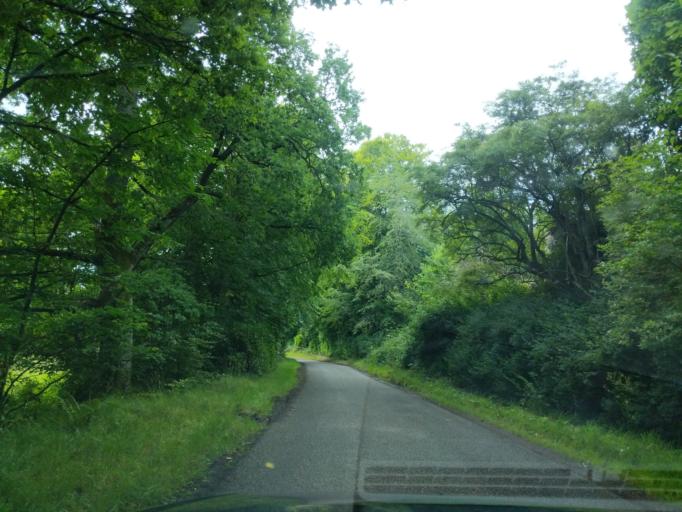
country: GB
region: Scotland
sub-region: Aberdeenshire
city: Aboyne
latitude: 57.0519
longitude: -2.8669
